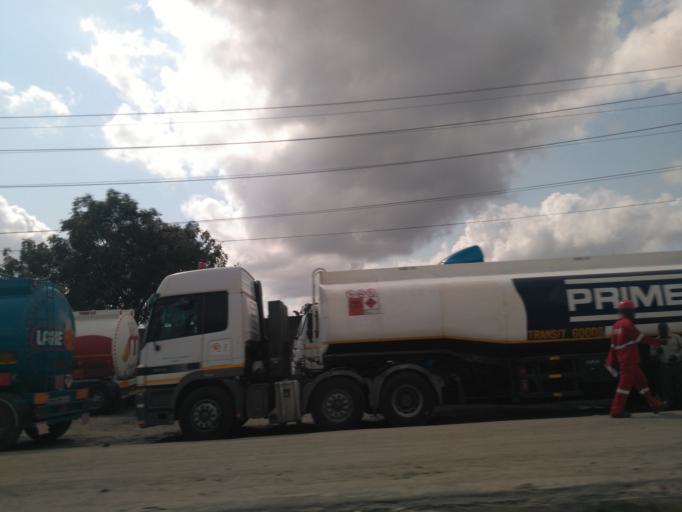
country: TZ
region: Dar es Salaam
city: Dar es Salaam
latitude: -6.8448
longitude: 39.2926
